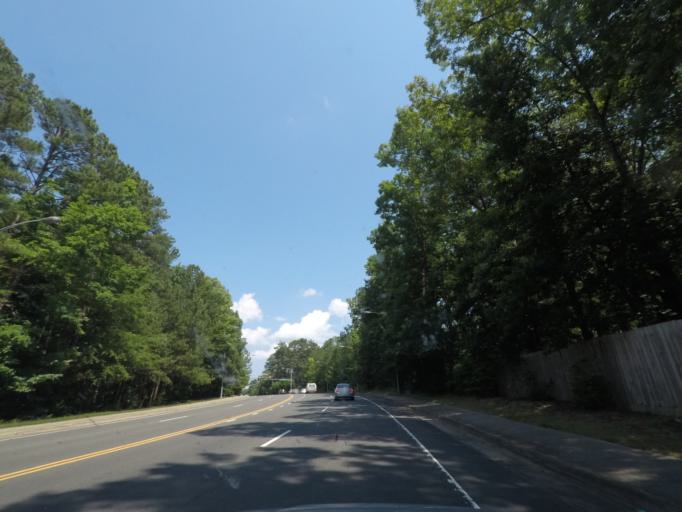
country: US
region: North Carolina
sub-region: Durham County
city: Durham
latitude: 35.9589
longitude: -78.9492
